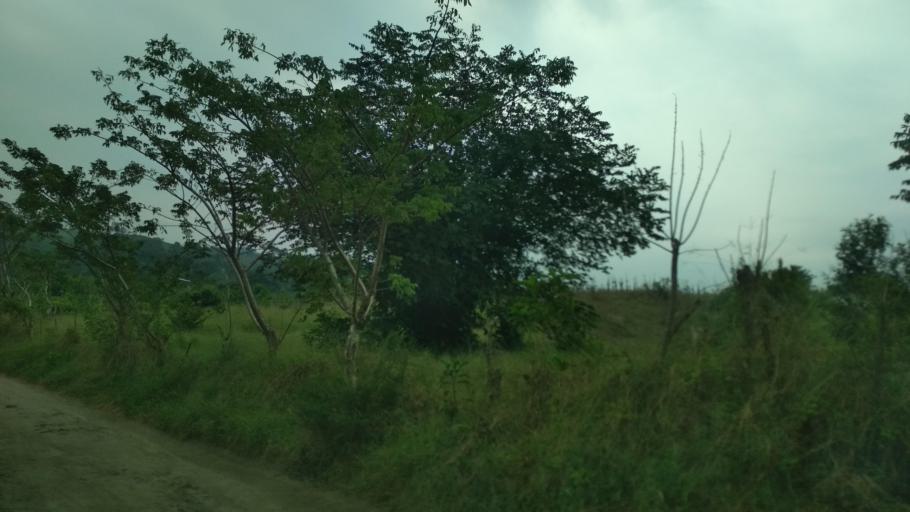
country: MM
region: Kayah
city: Loikaw
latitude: 20.2159
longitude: 97.3320
